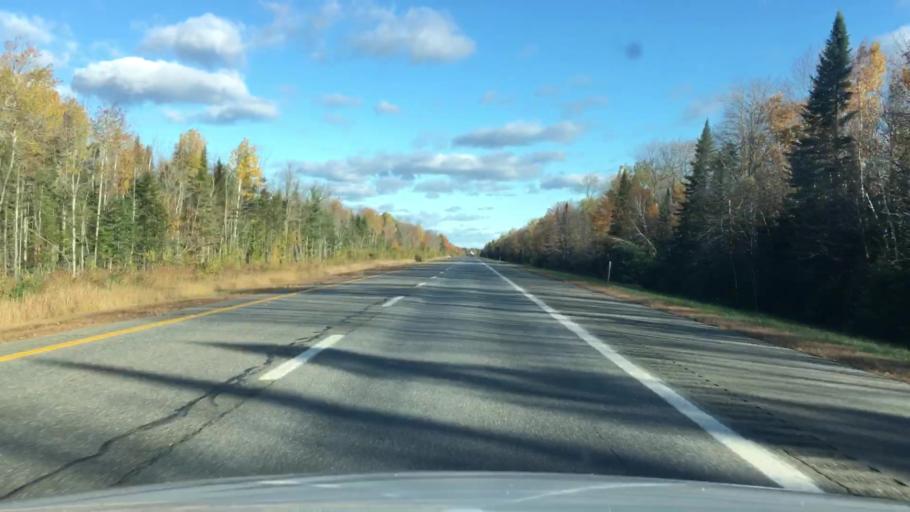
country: US
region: Maine
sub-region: Penobscot County
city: Greenbush
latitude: 45.0801
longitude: -68.6921
